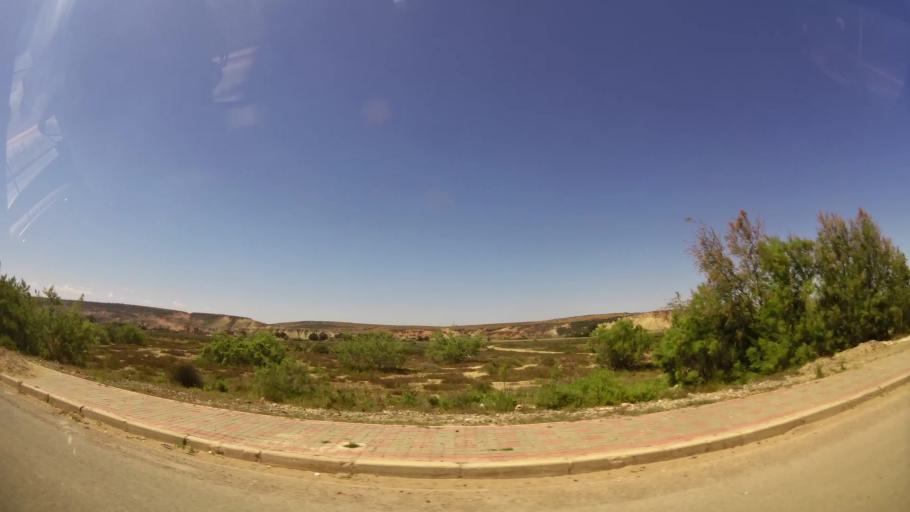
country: MA
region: Oriental
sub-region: Berkane-Taourirt
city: Madagh
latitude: 35.0997
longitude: -2.3075
